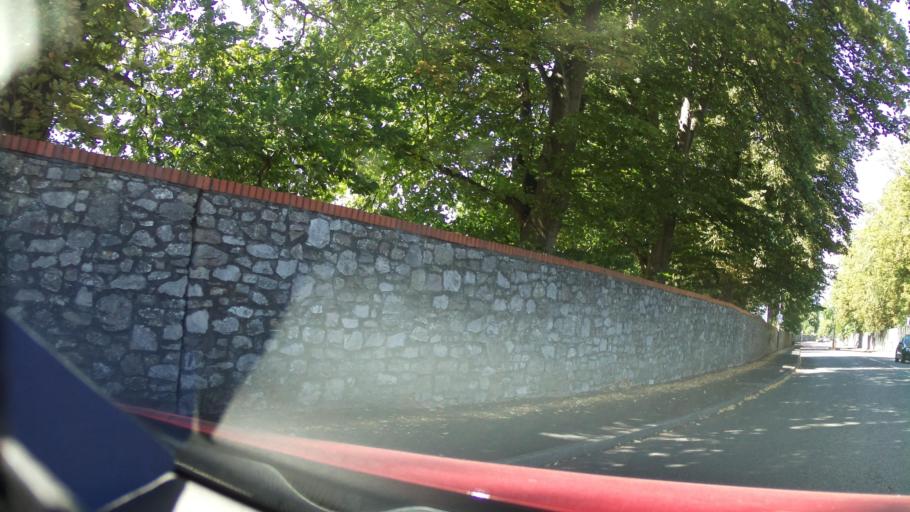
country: GB
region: England
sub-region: Bristol
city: Bristol
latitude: 51.4854
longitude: -2.6160
